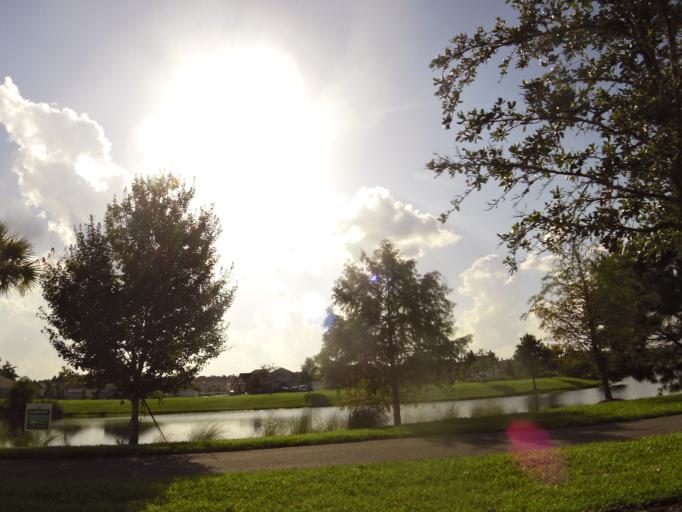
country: US
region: Florida
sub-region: Clay County
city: Green Cove Springs
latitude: 30.0271
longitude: -81.6306
